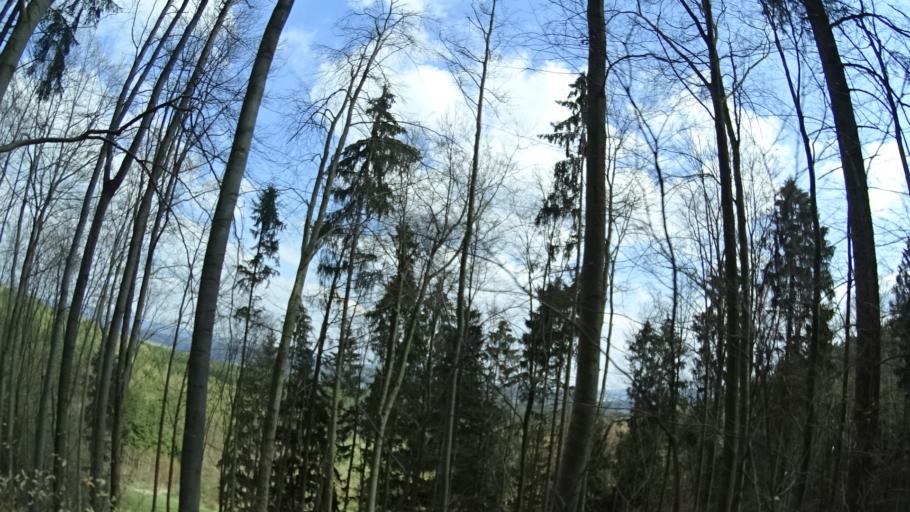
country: DE
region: Thuringia
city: Frankenhain
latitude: 50.7511
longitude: 10.7785
